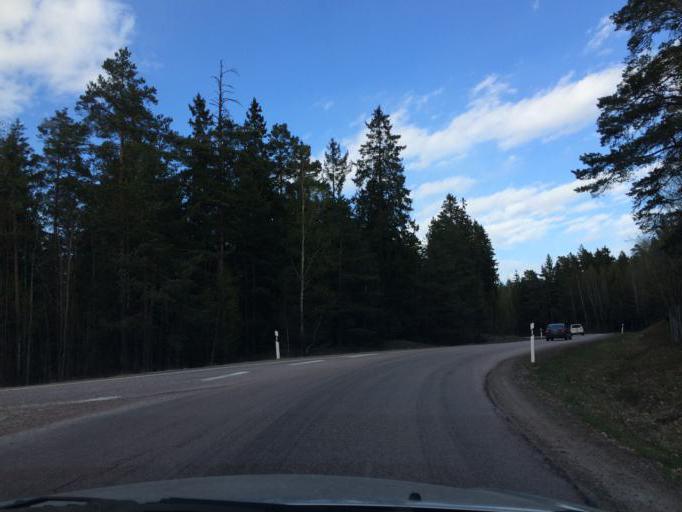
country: SE
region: Vaestmanland
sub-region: Hallstahammars Kommun
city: Kolback
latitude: 59.5790
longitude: 16.3533
